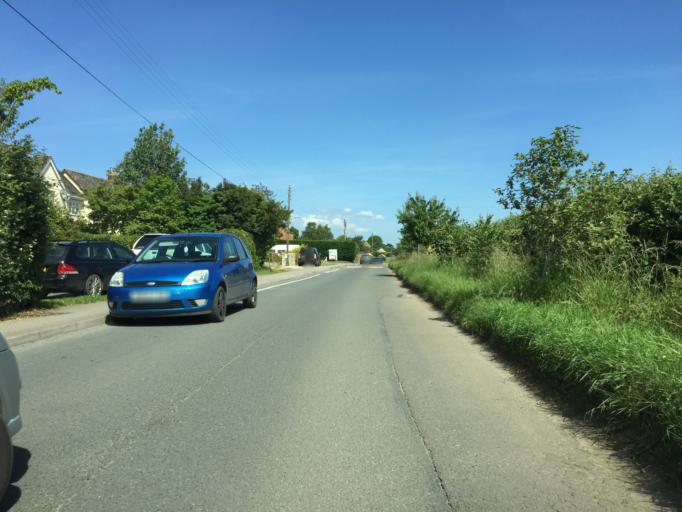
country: GB
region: England
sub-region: Gloucestershire
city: Dursley
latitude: 51.7252
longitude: -2.3751
